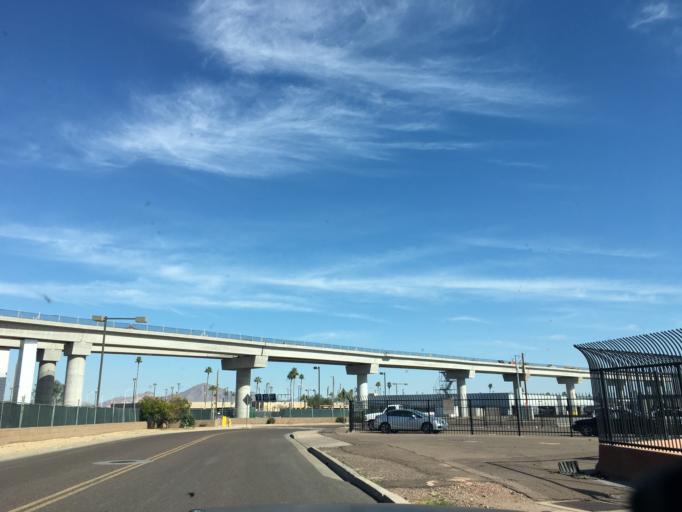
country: US
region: Arizona
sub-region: Maricopa County
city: Phoenix
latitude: 33.4350
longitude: -112.0171
